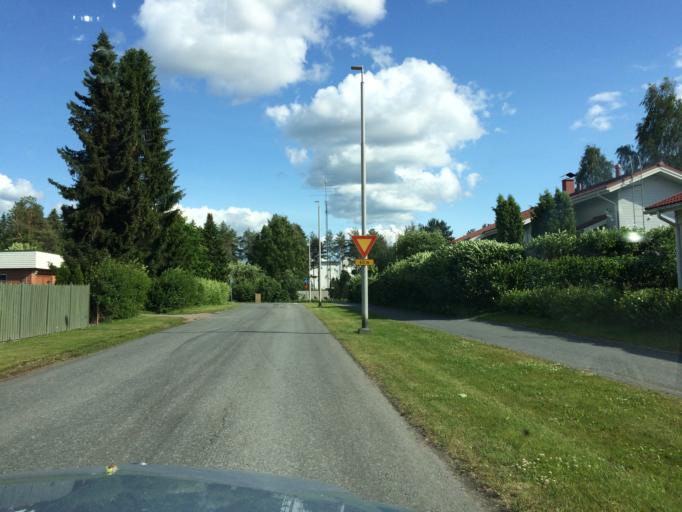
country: FI
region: Haeme
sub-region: Haemeenlinna
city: Haemeenlinna
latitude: 60.9836
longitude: 24.4011
